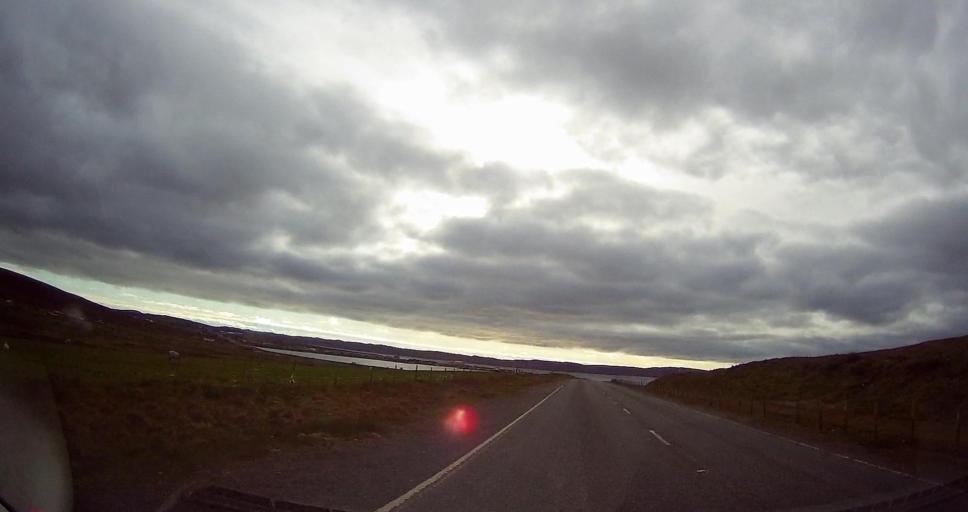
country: GB
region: Scotland
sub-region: Shetland Islands
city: Lerwick
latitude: 60.4447
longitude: -1.2429
